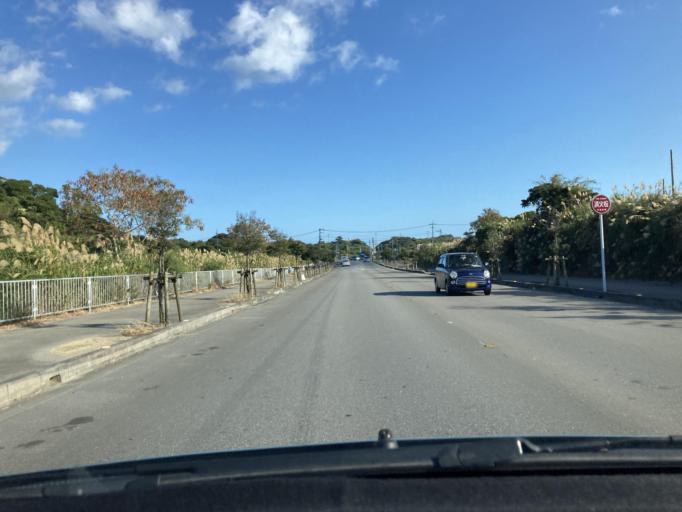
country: JP
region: Okinawa
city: Gushikawa
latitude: 26.3867
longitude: 127.8426
